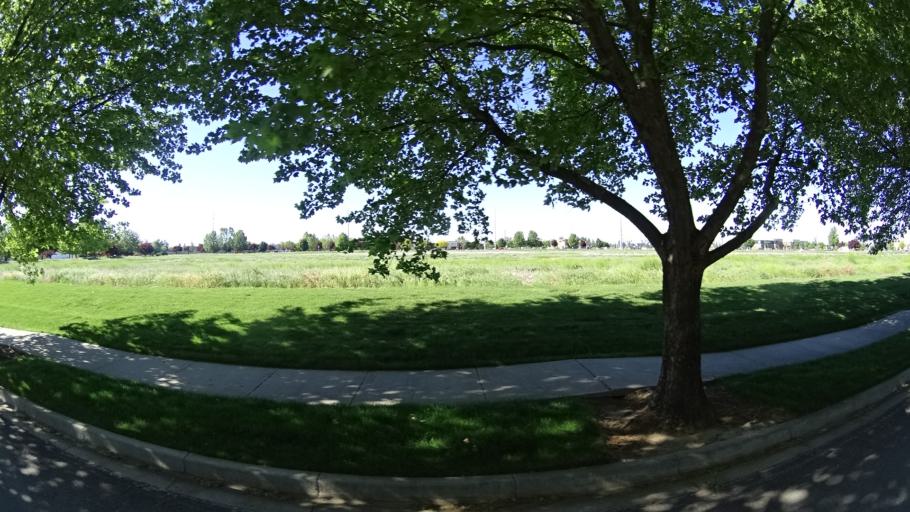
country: US
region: Idaho
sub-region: Ada County
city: Meridian
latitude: 43.6508
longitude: -116.4314
